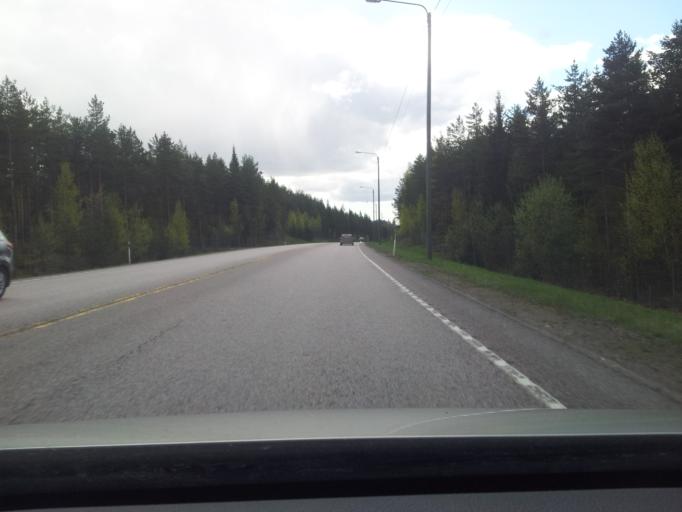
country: FI
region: Uusimaa
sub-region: Loviisa
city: Perna
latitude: 60.5073
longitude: 25.9659
